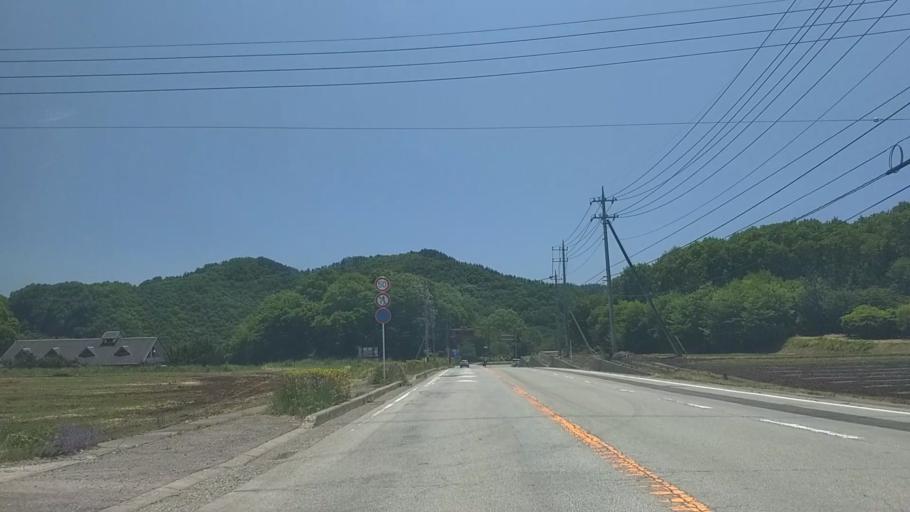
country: JP
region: Yamanashi
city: Nirasaki
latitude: 35.8801
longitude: 138.4398
